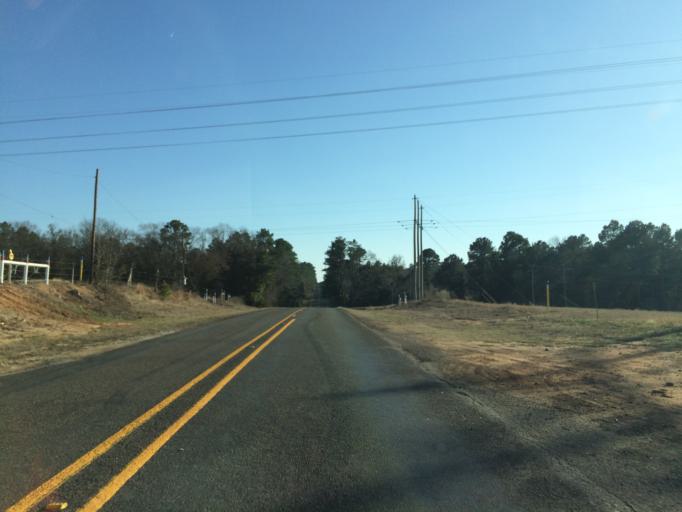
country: US
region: Texas
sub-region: Wood County
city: Hawkins
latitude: 32.6395
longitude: -95.3132
